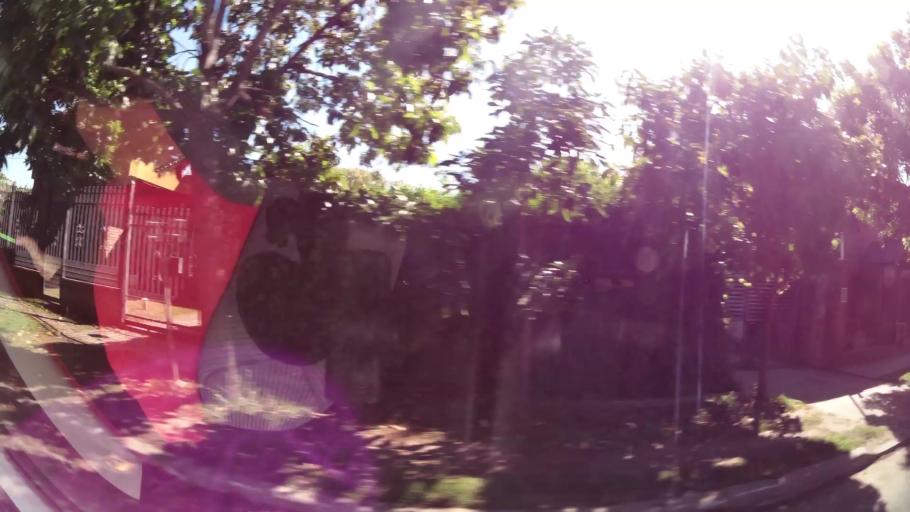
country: AR
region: Buenos Aires
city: Santa Catalina - Dique Lujan
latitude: -34.4916
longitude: -58.6915
